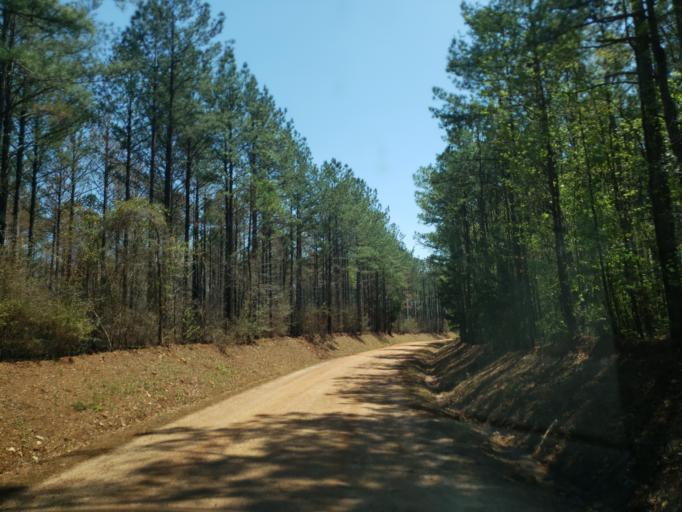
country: US
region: Alabama
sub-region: Tallapoosa County
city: Camp Hill
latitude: 32.6490
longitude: -85.6478
